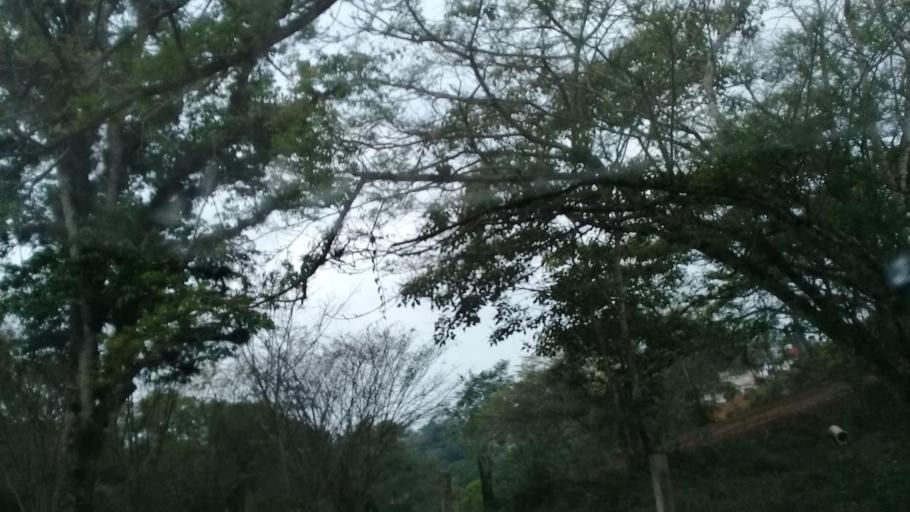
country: MX
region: Veracruz
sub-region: Xalapa
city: Fraccionamiento las Fuentes
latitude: 19.4940
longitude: -96.8962
